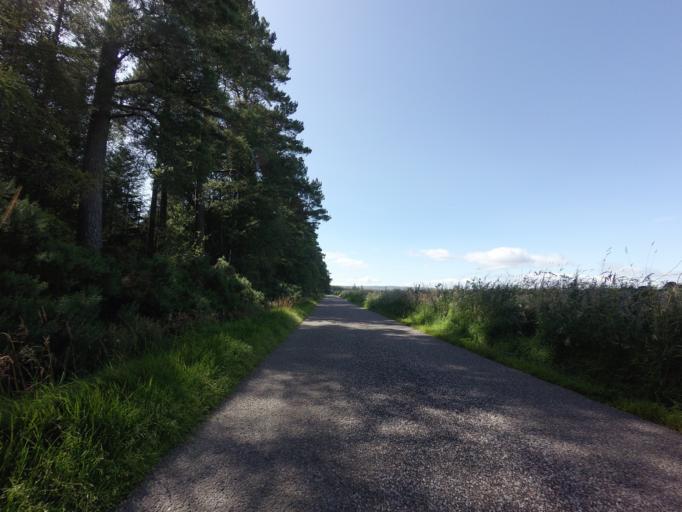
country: GB
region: Scotland
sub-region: Highland
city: Nairn
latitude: 57.5252
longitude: -3.8635
